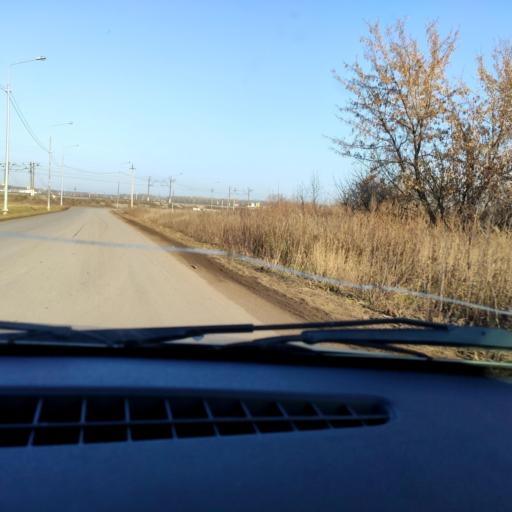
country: RU
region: Bashkortostan
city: Kabakovo
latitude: 54.6383
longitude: 56.0765
